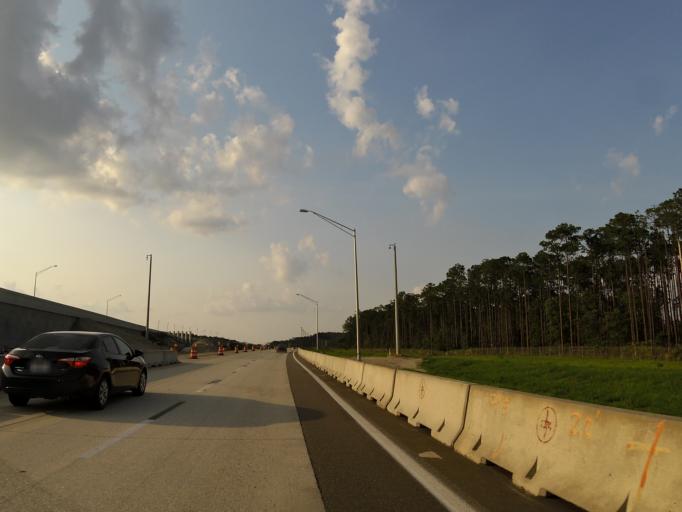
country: US
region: Florida
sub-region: Saint Johns County
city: Palm Valley
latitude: 30.1771
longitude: -81.5136
